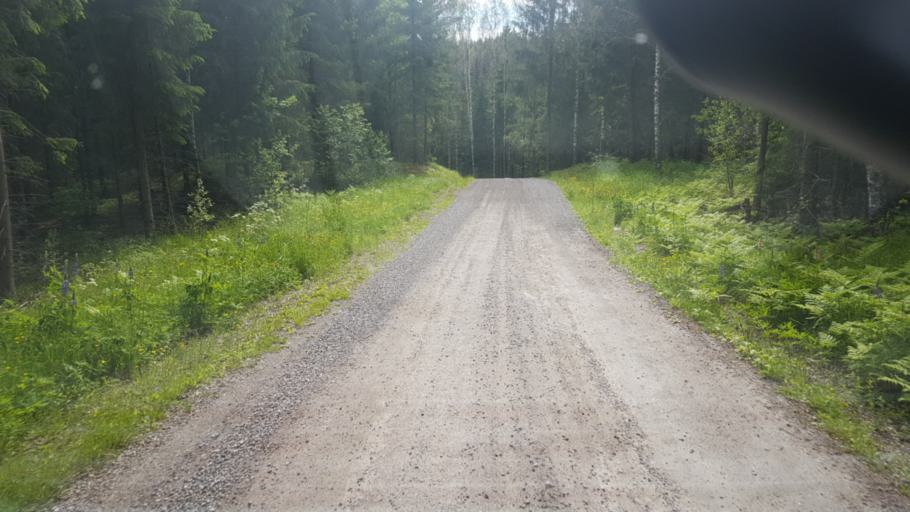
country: SE
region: Vaermland
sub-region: Eda Kommun
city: Amotfors
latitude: 59.8237
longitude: 12.4084
